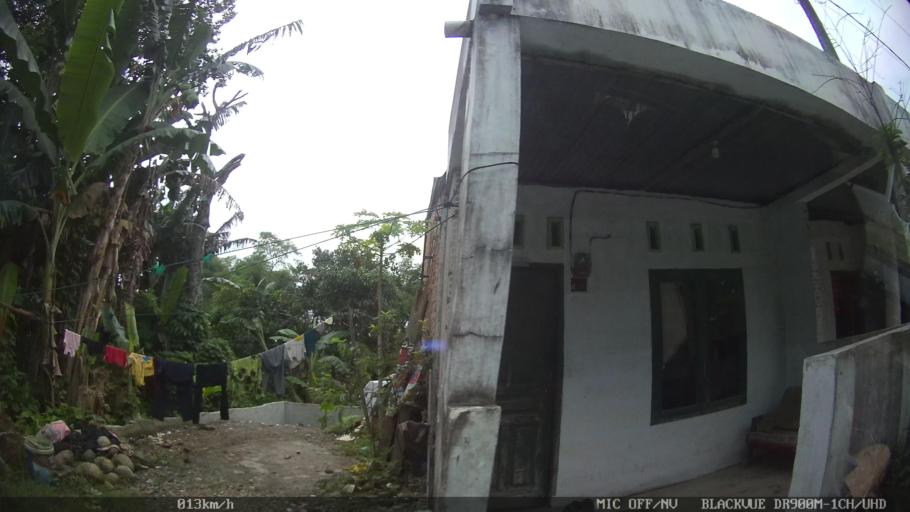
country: ID
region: North Sumatra
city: Sunggal
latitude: 3.6462
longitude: 98.5930
